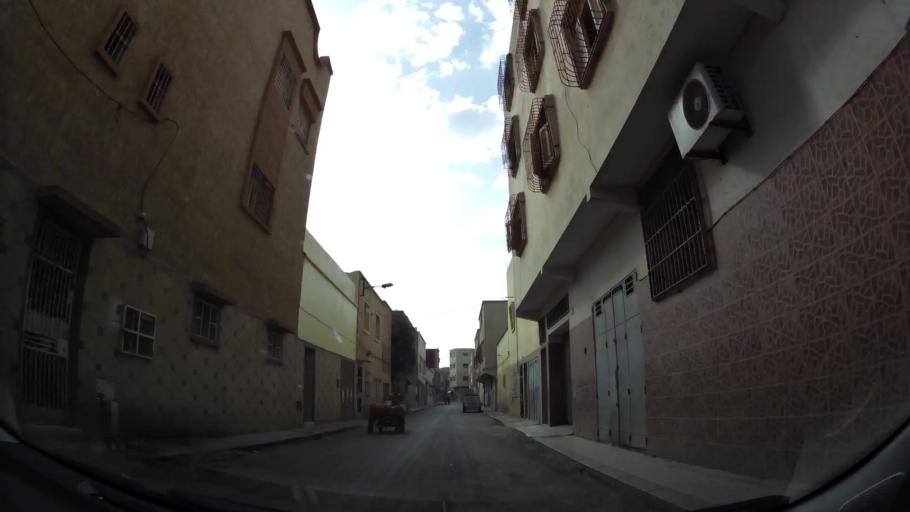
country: MA
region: Oriental
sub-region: Oujda-Angad
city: Oujda
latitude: 34.6889
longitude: -1.9065
